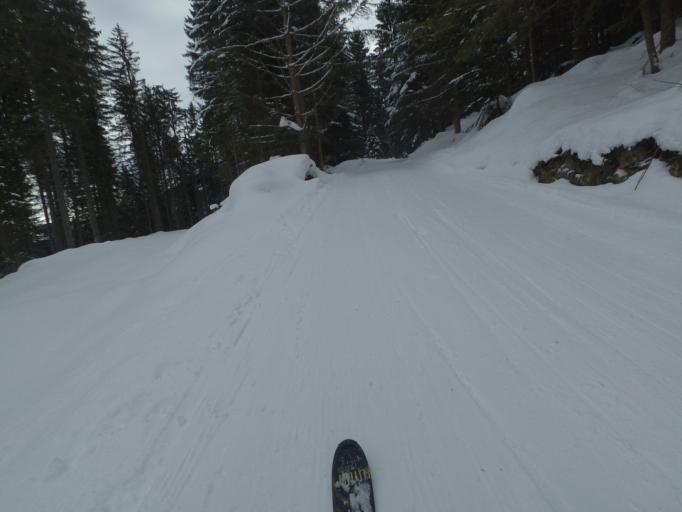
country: AT
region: Salzburg
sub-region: Politischer Bezirk Sankt Johann im Pongau
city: Sankt Johann im Pongau
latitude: 47.3205
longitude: 13.2212
